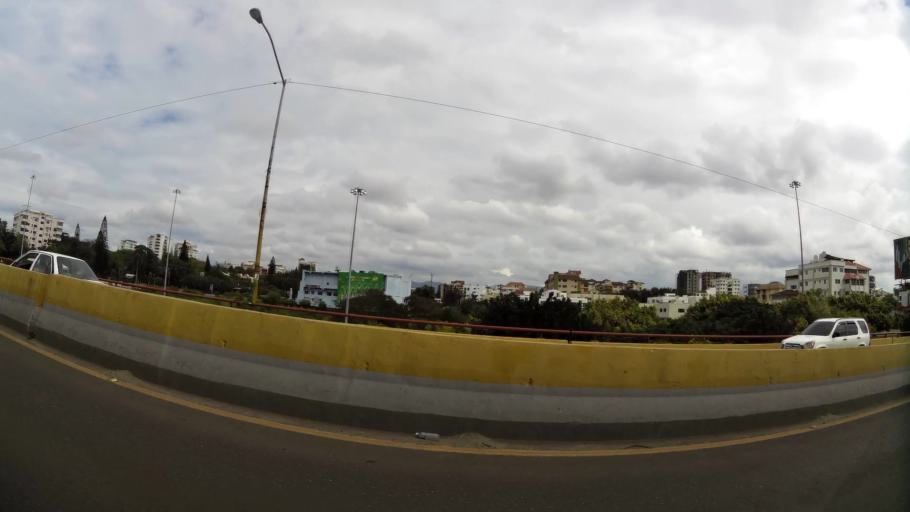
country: DO
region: Santiago
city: Santiago de los Caballeros
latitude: 19.4495
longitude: -70.6849
